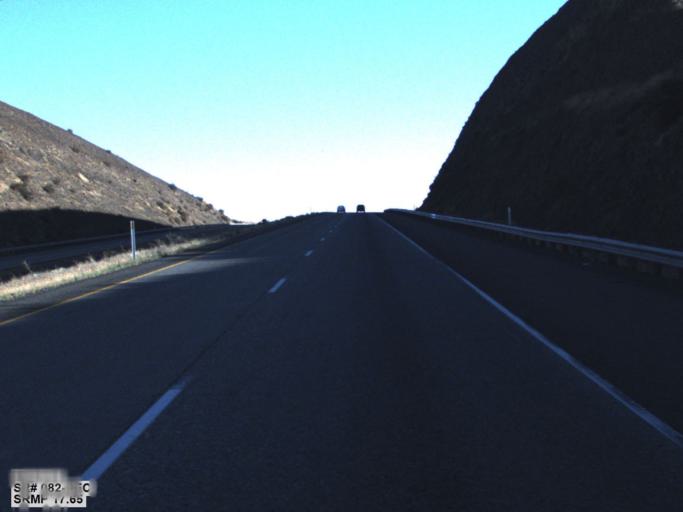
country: US
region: Washington
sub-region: Yakima County
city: Terrace Heights
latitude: 46.7671
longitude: -120.3777
